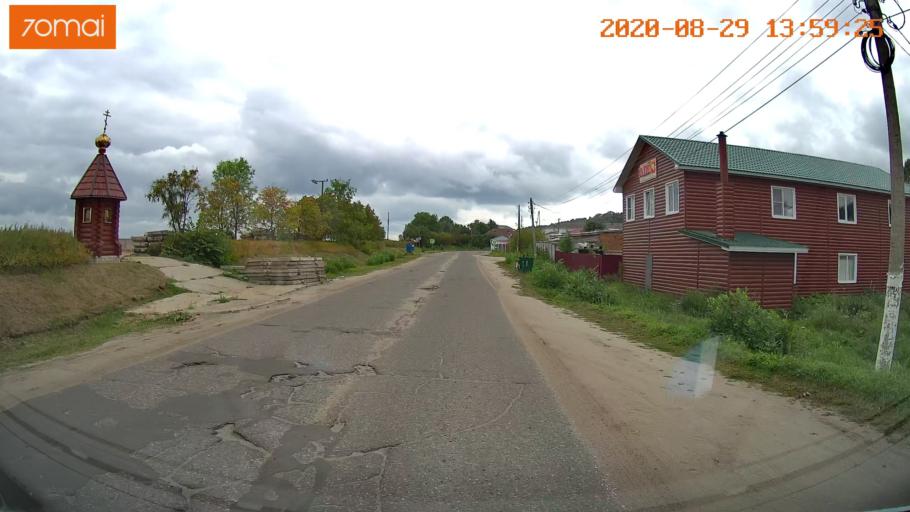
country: RU
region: Ivanovo
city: Yur'yevets
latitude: 57.3158
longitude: 43.1122
